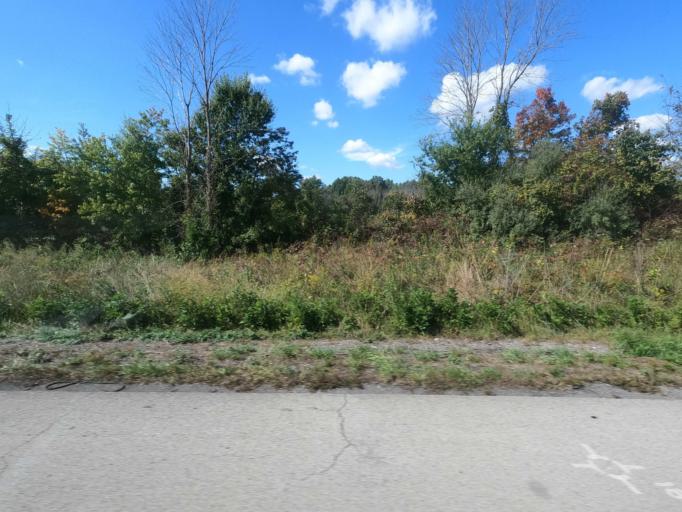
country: US
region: Illinois
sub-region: Jefferson County
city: Ina
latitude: 38.1743
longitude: -88.9062
